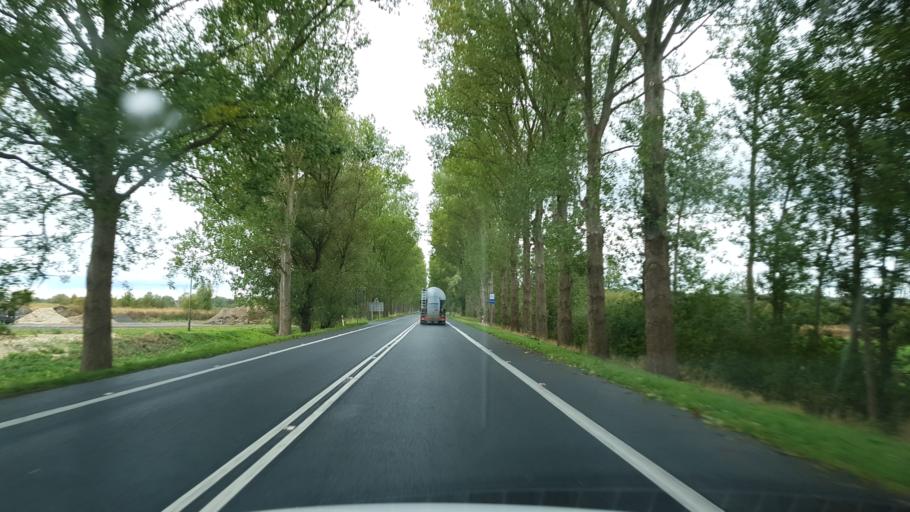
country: PL
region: West Pomeranian Voivodeship
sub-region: Powiat kamienski
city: Wolin
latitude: 53.8501
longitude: 14.5985
